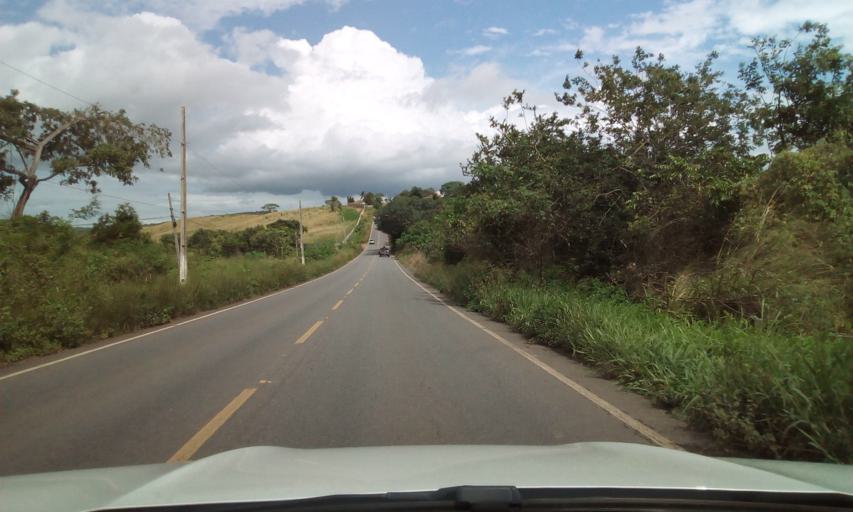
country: BR
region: Paraiba
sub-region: Guarabira
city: Guarabira
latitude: -6.8770
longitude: -35.5009
